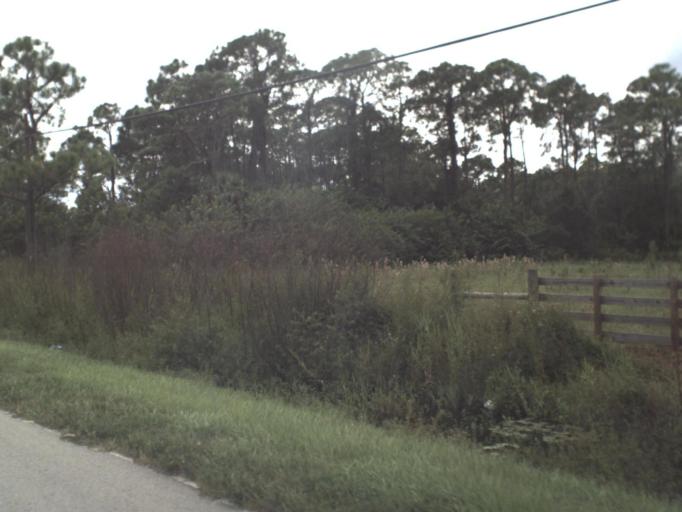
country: US
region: Florida
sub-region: Lee County
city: Fort Myers Shores
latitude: 26.7694
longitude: -81.7608
